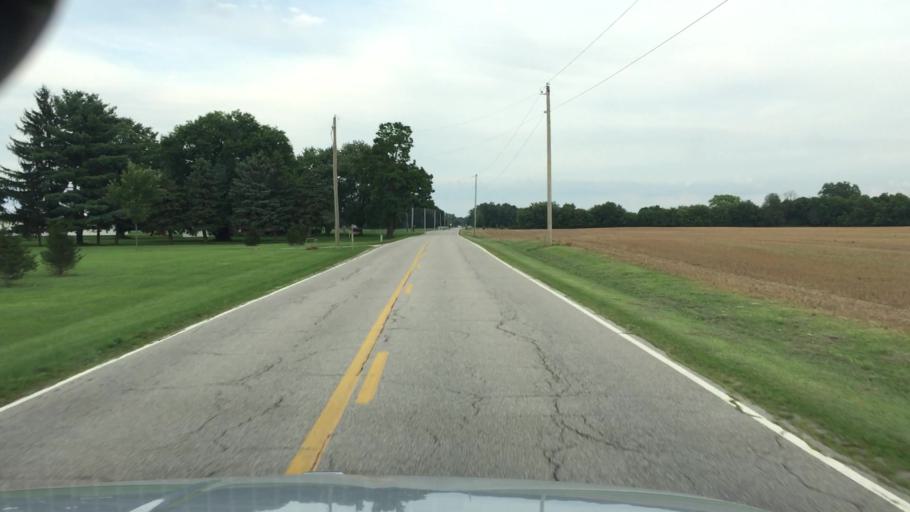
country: US
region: Ohio
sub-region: Madison County
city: Plain City
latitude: 40.0740
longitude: -83.2382
